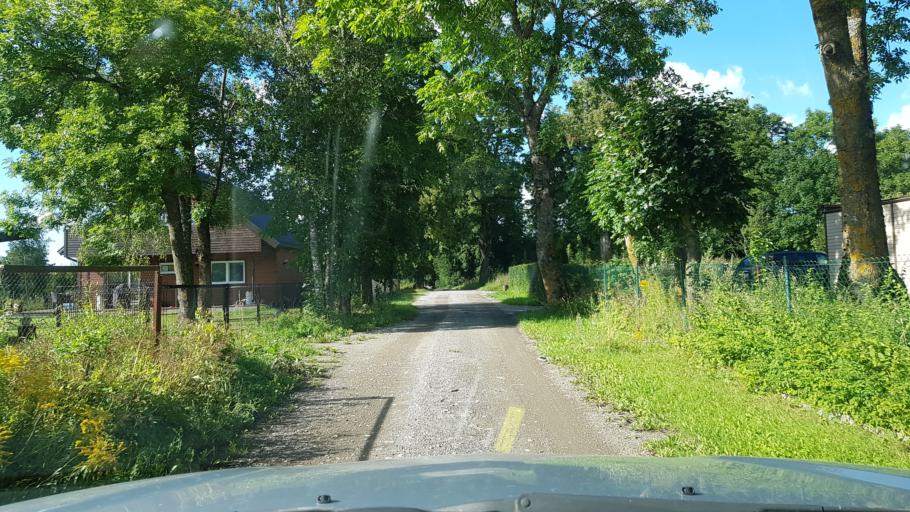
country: EE
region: Harju
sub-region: Rae vald
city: Jueri
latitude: 59.3698
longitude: 24.8380
